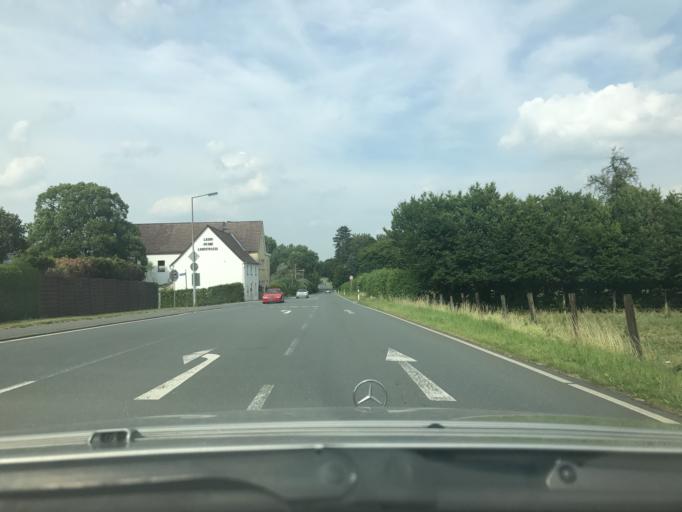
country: DE
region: North Rhine-Westphalia
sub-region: Regierungsbezirk Arnsberg
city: Holzwickede
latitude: 51.4514
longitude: 7.6817
